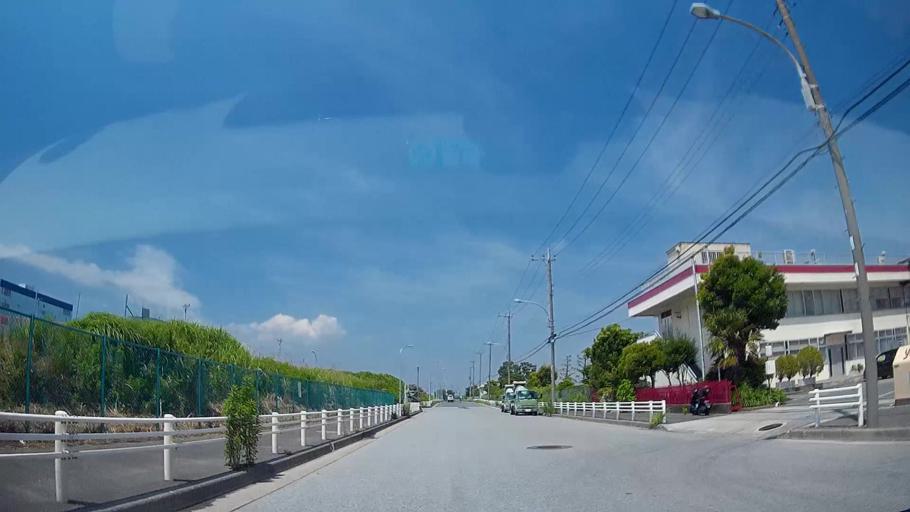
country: JP
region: Tokyo
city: Urayasu
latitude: 35.6305
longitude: 139.8337
